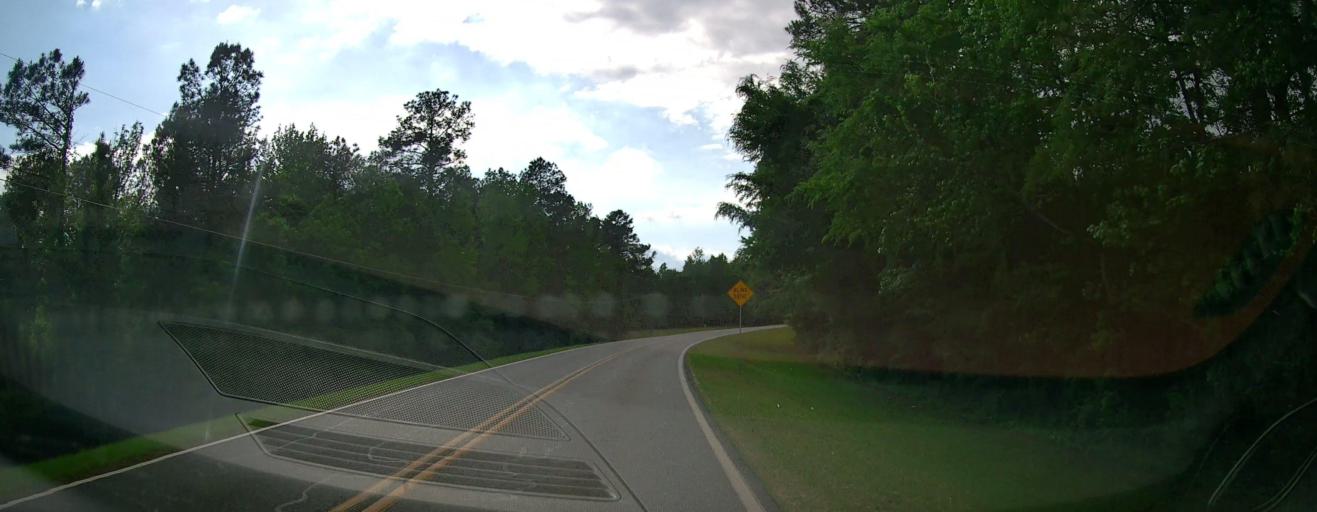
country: US
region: Georgia
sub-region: Baldwin County
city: Hardwick
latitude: 33.0640
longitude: -83.1678
